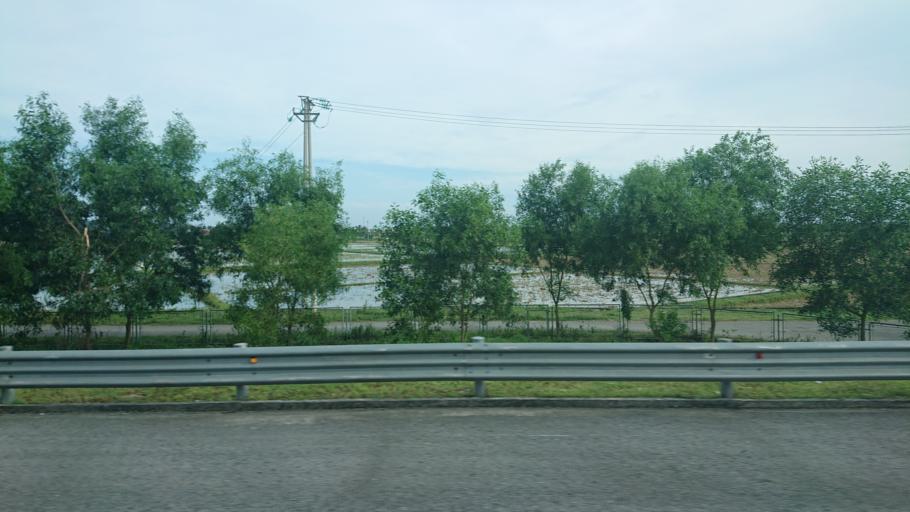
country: VN
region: Hai Phong
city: Nui Doi
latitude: 20.7658
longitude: 106.6493
